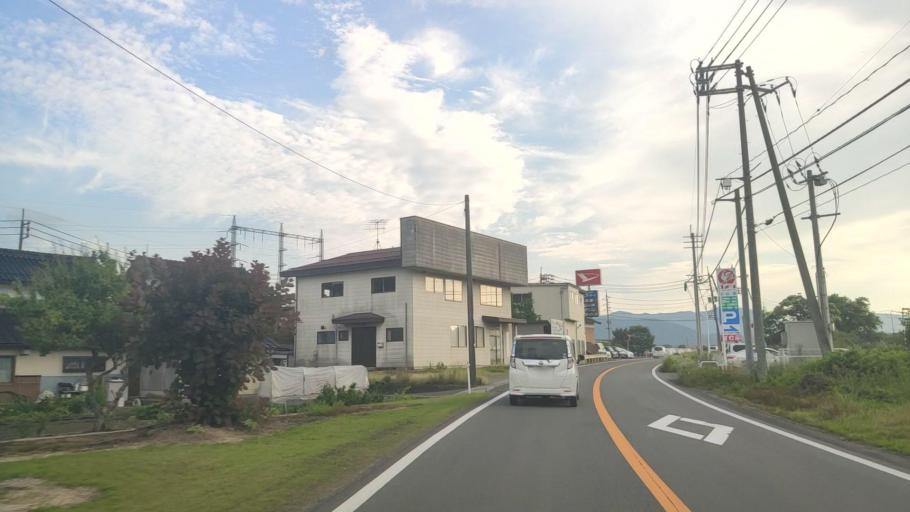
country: JP
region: Tottori
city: Kurayoshi
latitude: 35.2829
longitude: 133.6950
